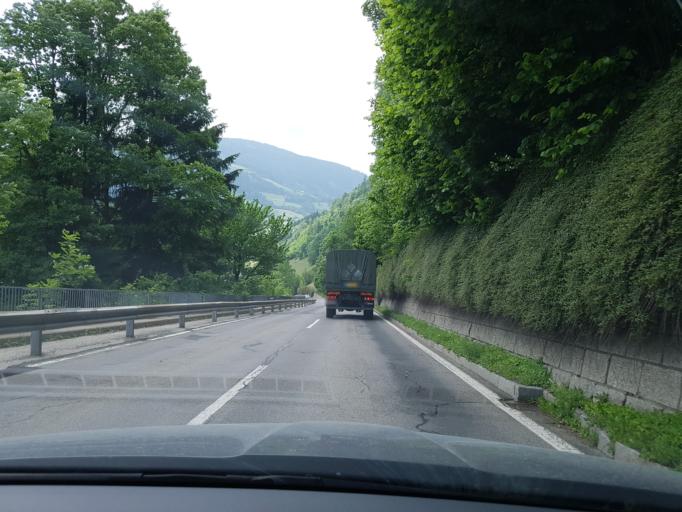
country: AT
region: Carinthia
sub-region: Politischer Bezirk Spittal an der Drau
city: Radenthein
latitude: 46.7991
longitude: 13.7213
